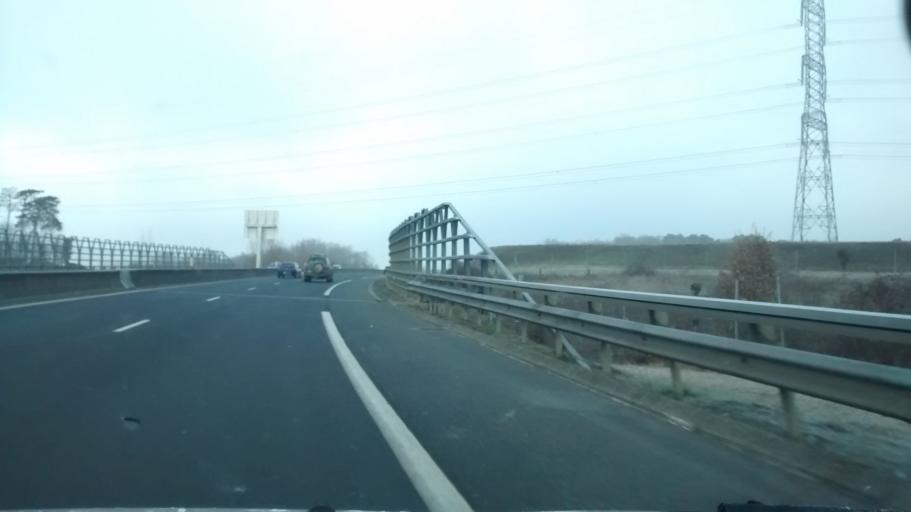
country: FR
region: Centre
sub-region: Departement d'Indre-et-Loire
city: Chambray-les-Tours
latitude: 47.3228
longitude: 0.6976
